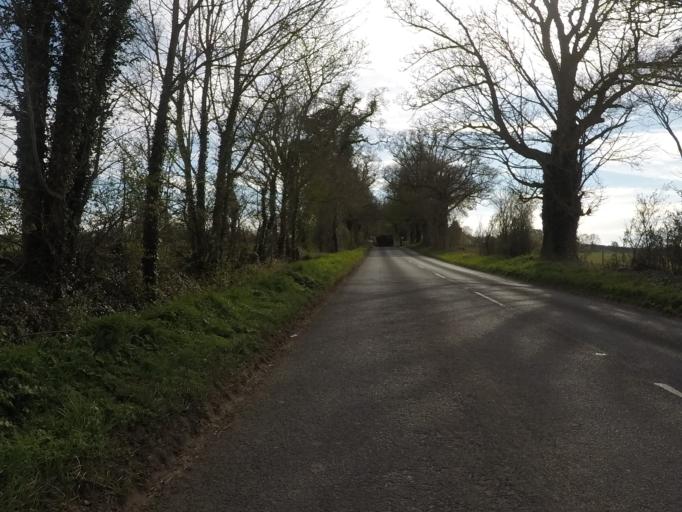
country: GB
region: England
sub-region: Oxfordshire
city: Charlbury
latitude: 51.8503
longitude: -1.4734
